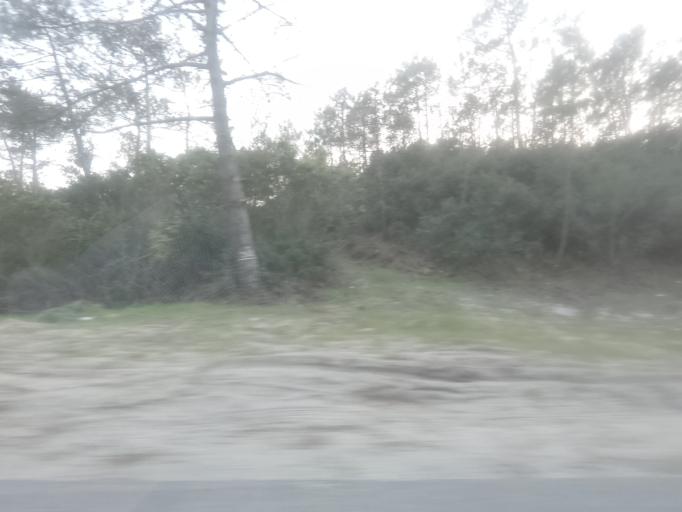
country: PT
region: Leiria
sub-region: Alcobaca
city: Pataias
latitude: 39.7540
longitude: -9.0238
